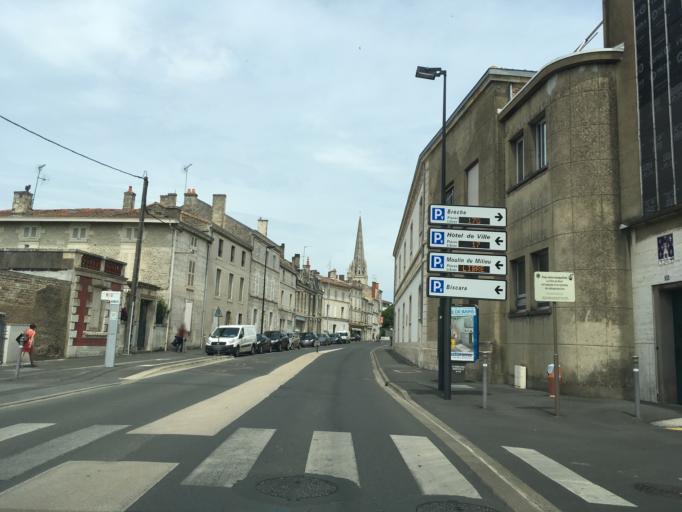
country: FR
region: Poitou-Charentes
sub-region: Departement des Deux-Sevres
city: Niort
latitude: 46.3195
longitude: -0.4655
